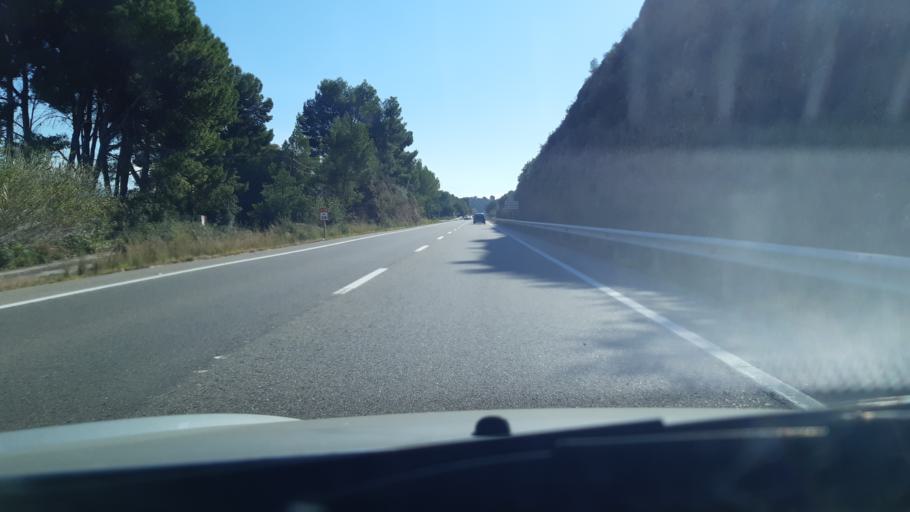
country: ES
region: Catalonia
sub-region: Provincia de Tarragona
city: Tivenys
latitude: 40.8937
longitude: 0.4892
